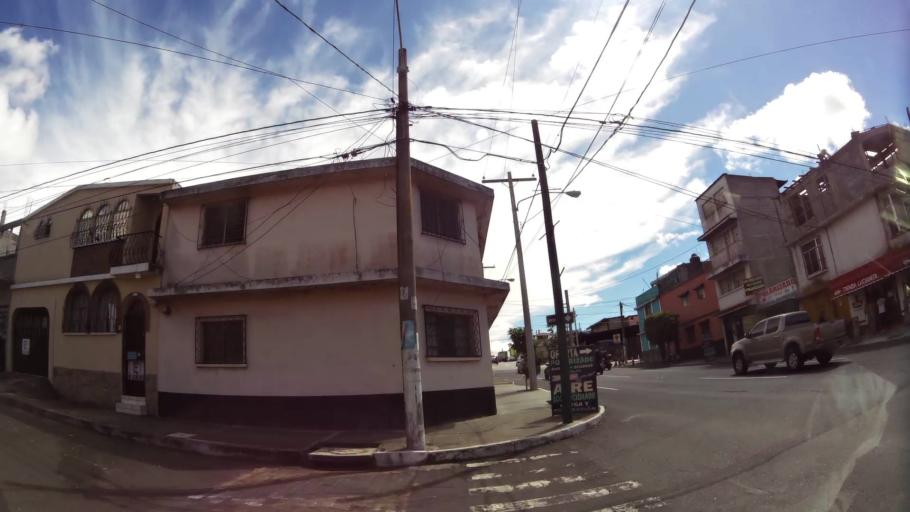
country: GT
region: Guatemala
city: Guatemala City
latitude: 14.6039
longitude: -90.5415
